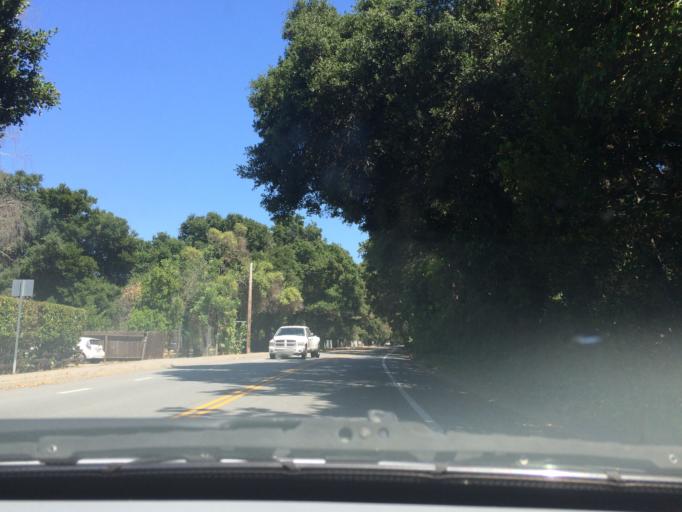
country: US
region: California
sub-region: San Mateo County
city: North Fair Oaks
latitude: 37.4752
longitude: -122.1745
